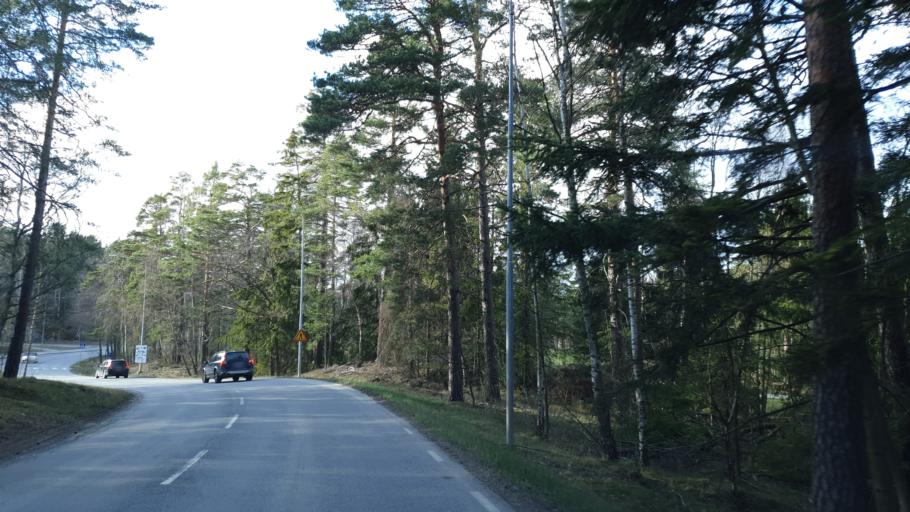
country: SE
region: Stockholm
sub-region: Lidingo
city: Lidingoe
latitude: 59.3812
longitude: 18.1224
